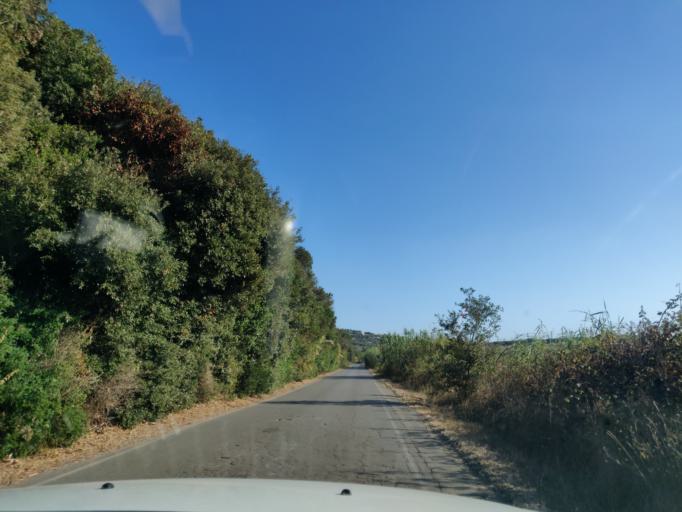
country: IT
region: Tuscany
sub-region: Provincia di Grosseto
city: Orbetello Scalo
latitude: 42.4255
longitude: 11.2817
